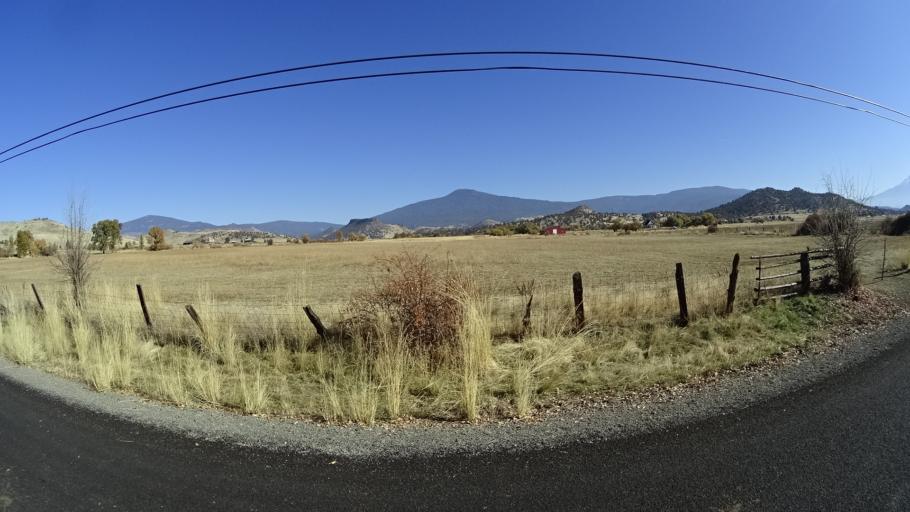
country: US
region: California
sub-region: Siskiyou County
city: Montague
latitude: 41.7232
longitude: -122.3891
